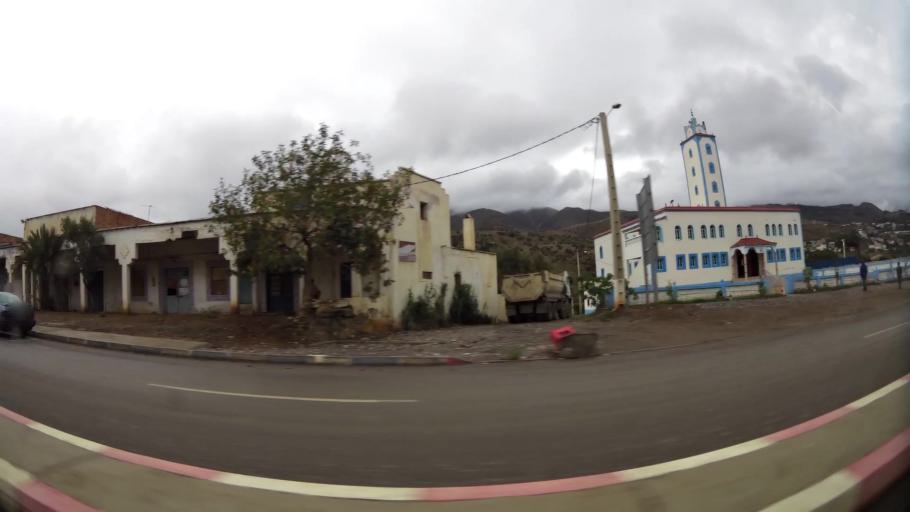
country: MA
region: Taza-Al Hoceima-Taounate
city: Imzourene
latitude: 34.9660
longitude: -3.8140
